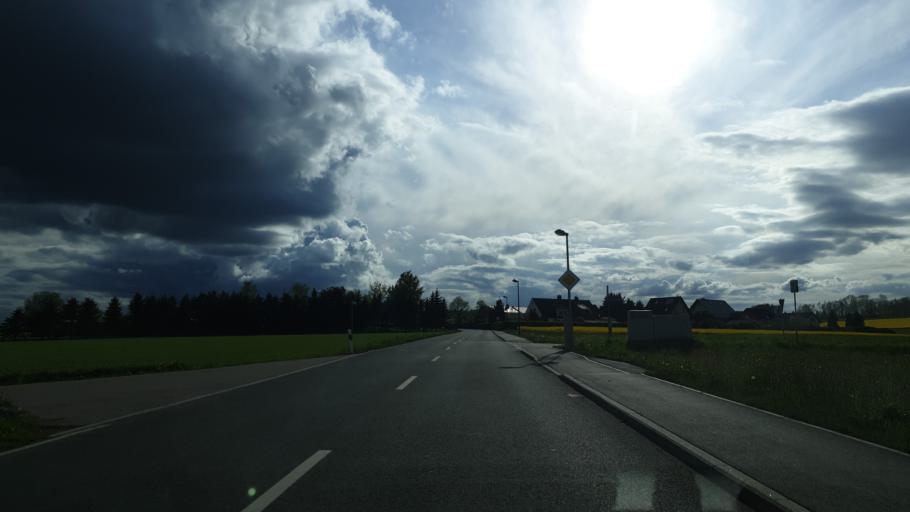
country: DE
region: Saxony
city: Oelsnitz
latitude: 50.6949
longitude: 12.7188
